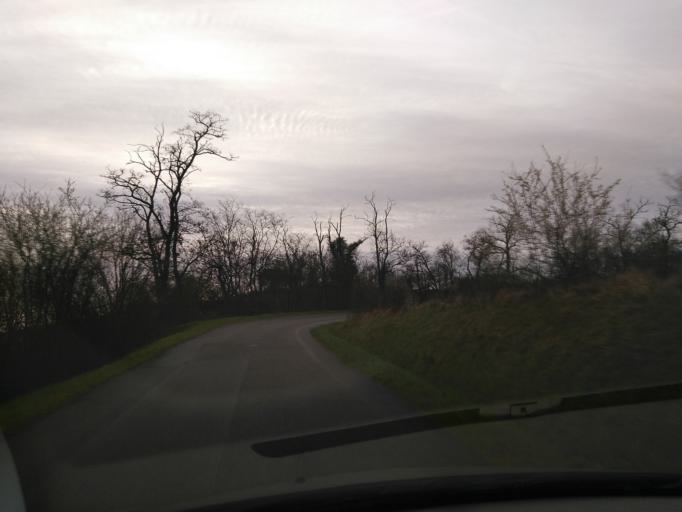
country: FR
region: Midi-Pyrenees
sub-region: Departement du Tarn-et-Garonne
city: Finhan
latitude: 43.8783
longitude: 1.1469
